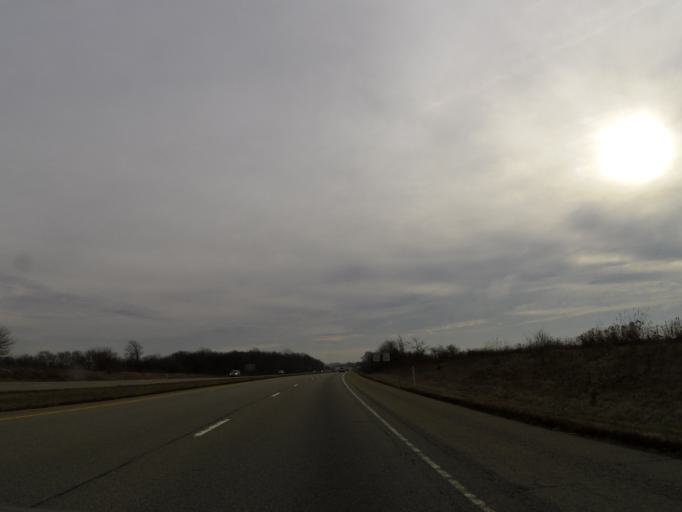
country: US
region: Indiana
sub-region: Fountain County
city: Veedersburg
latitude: 40.1238
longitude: -87.2318
